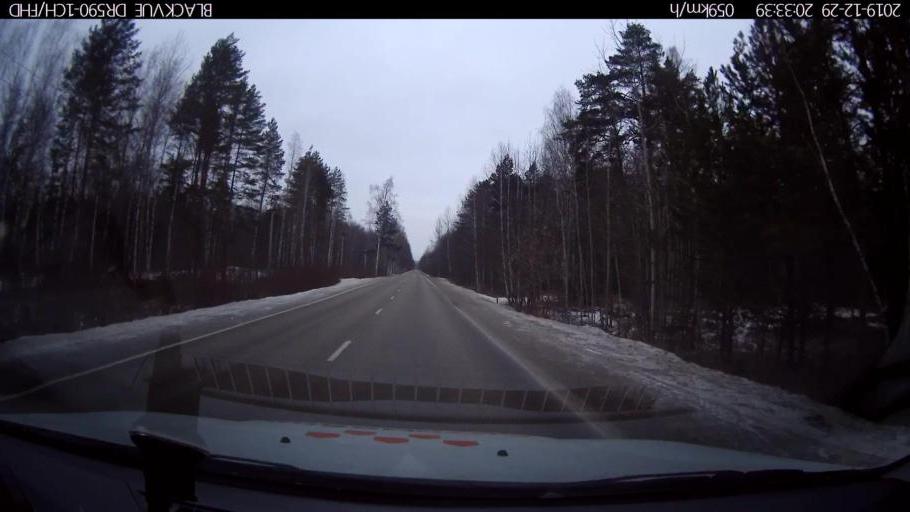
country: RU
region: Nizjnij Novgorod
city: Afonino
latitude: 56.1817
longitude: 44.0492
